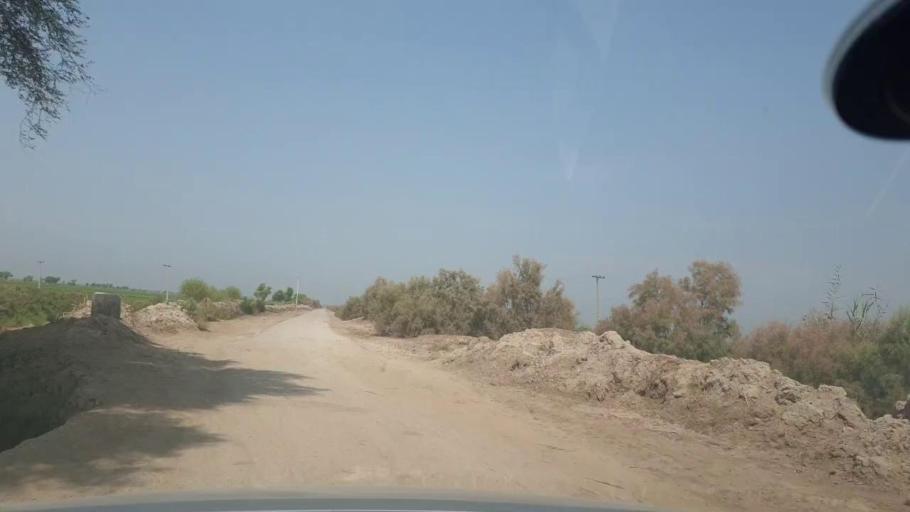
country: PK
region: Balochistan
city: Mehrabpur
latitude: 28.0578
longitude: 68.0746
